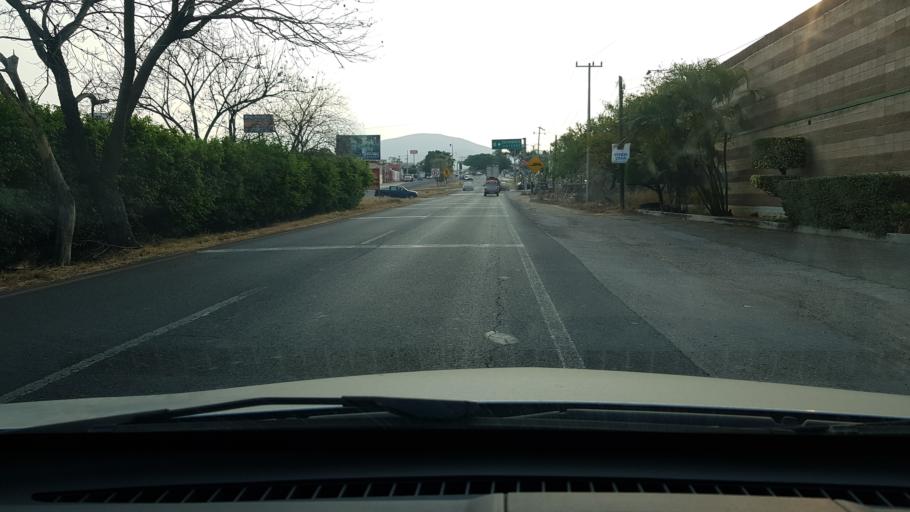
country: MX
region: Morelos
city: Yautepec
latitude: 18.8712
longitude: -99.0780
